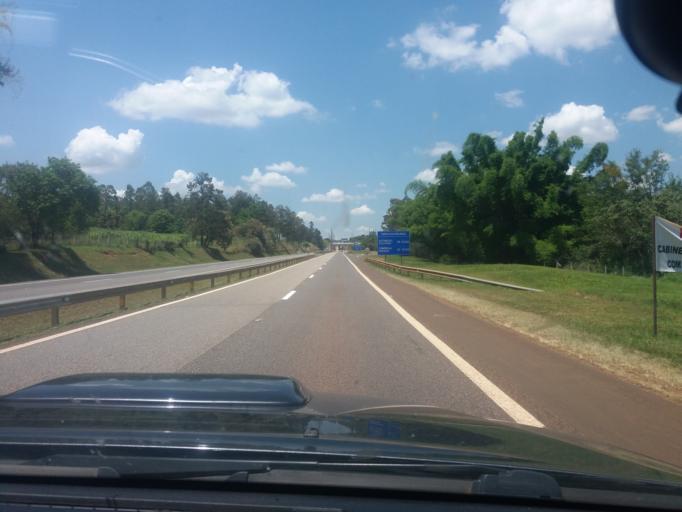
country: BR
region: Sao Paulo
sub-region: Itapetininga
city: Itapetininga
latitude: -23.4666
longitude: -47.9649
